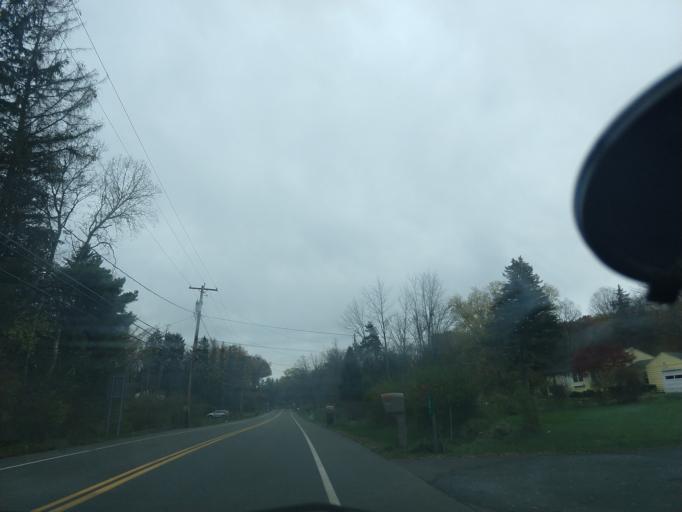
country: US
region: New York
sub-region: Tompkins County
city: East Ithaca
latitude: 42.4313
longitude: -76.4374
